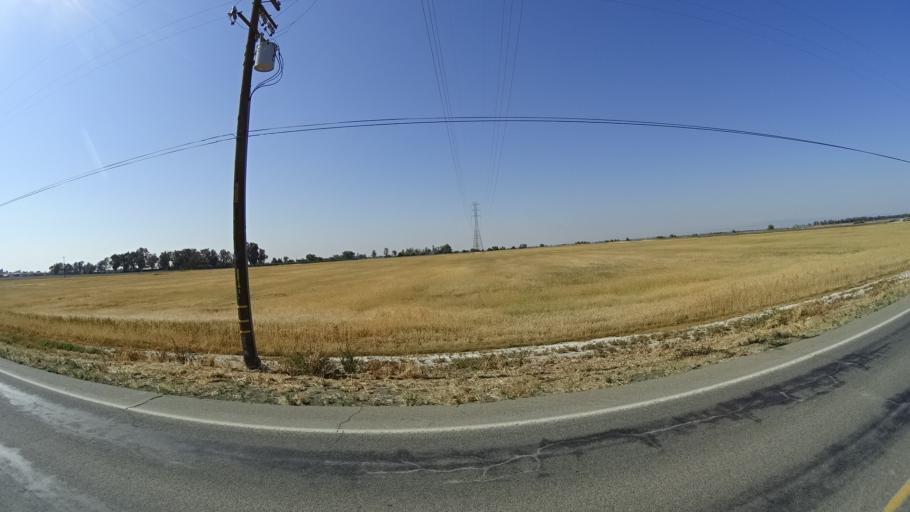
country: US
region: California
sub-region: Kings County
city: Lemoore Station
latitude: 36.3438
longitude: -119.8894
